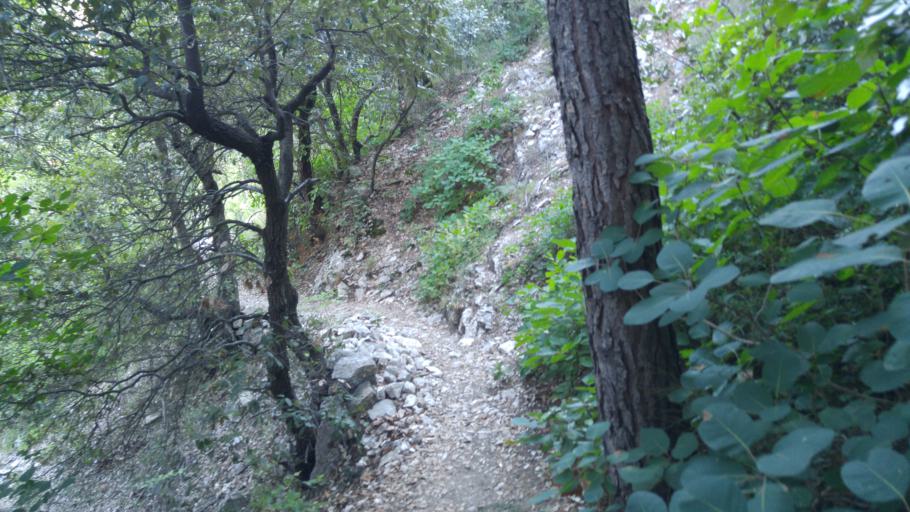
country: IT
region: The Marches
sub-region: Provincia di Pesaro e Urbino
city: Canavaccio
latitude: 43.6560
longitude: 12.7320
